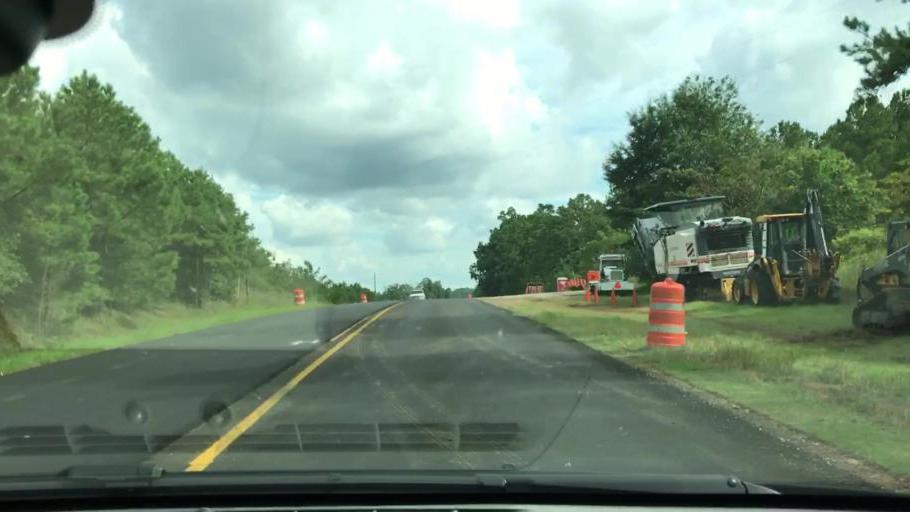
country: US
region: Georgia
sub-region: Clay County
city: Fort Gaines
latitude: 31.5902
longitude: -85.0324
